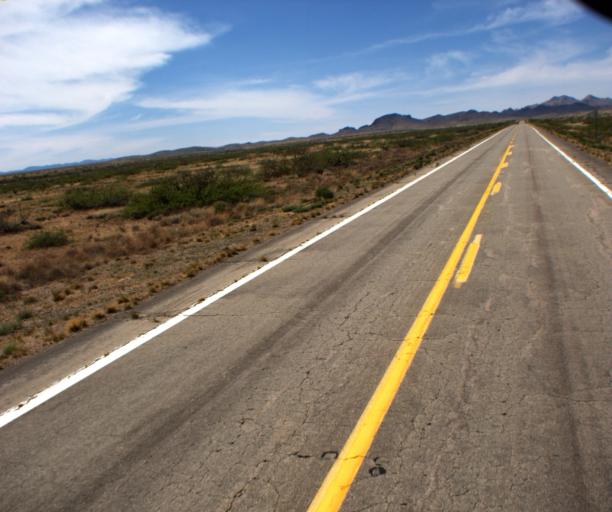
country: US
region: Arizona
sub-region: Cochise County
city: Willcox
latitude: 32.3762
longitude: -109.6433
